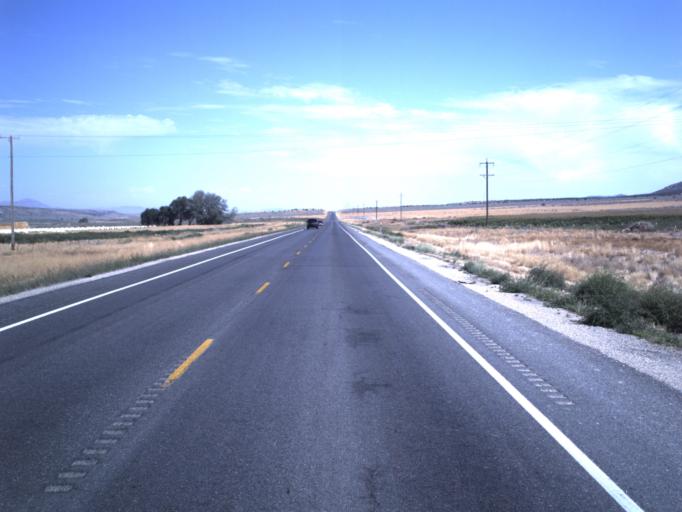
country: US
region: Utah
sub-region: Sanpete County
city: Gunnison
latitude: 39.2617
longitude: -111.8658
